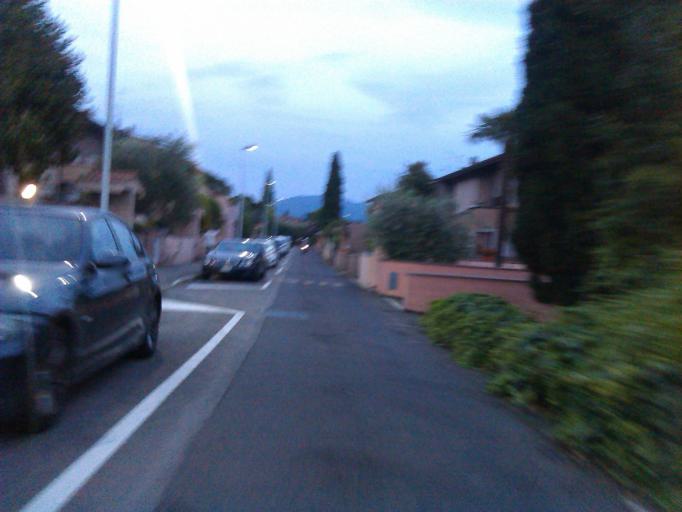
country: IT
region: Tuscany
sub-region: Province of Arezzo
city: Viciomaggio
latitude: 43.4429
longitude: 11.7801
